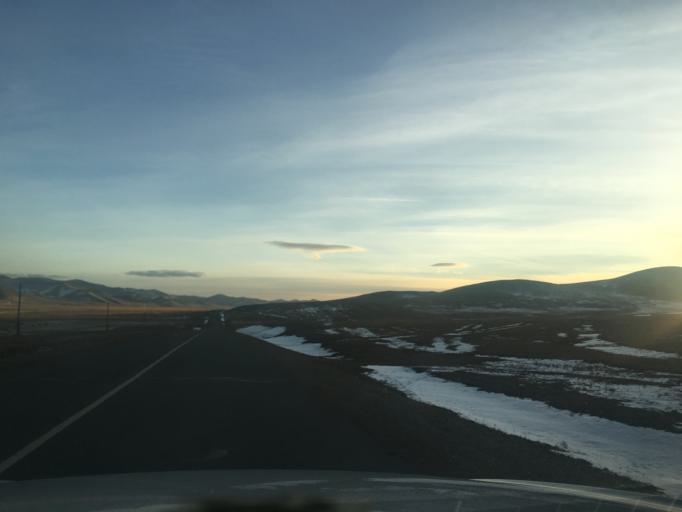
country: MN
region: Central Aimak
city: Mandal
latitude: 48.1873
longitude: 106.7051
